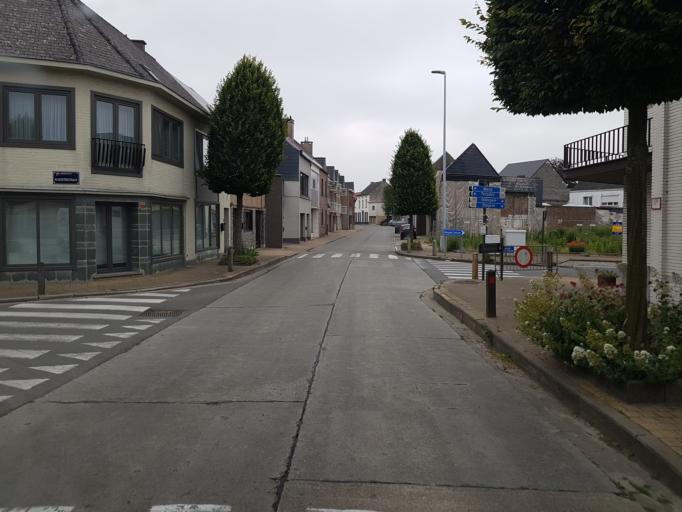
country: BE
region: Flanders
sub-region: Provincie Oost-Vlaanderen
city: Denderleeuw
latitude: 50.8755
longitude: 4.0484
